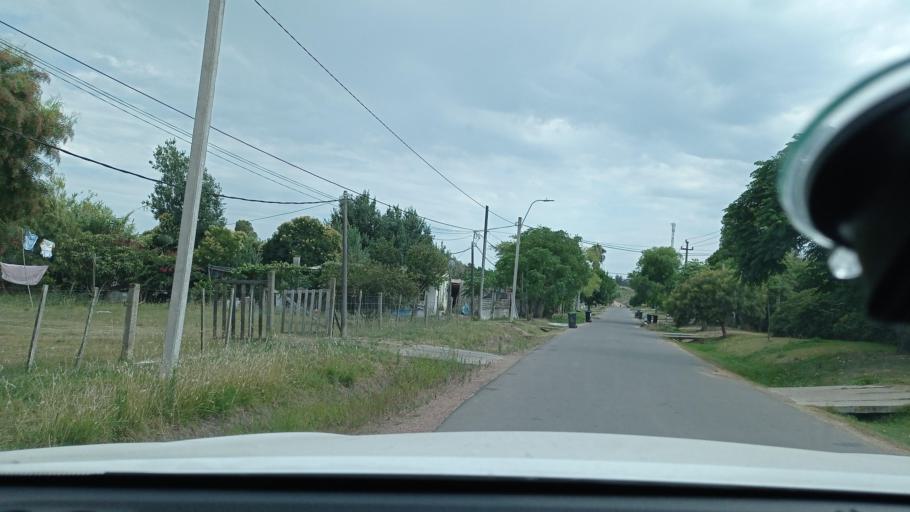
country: UY
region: Canelones
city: Pando
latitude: -34.7145
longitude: -55.9700
